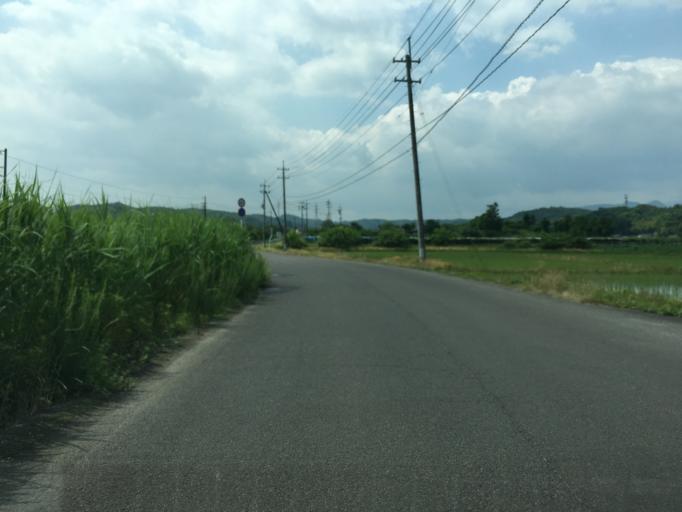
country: JP
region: Fukushima
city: Fukushima-shi
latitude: 37.7166
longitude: 140.4531
